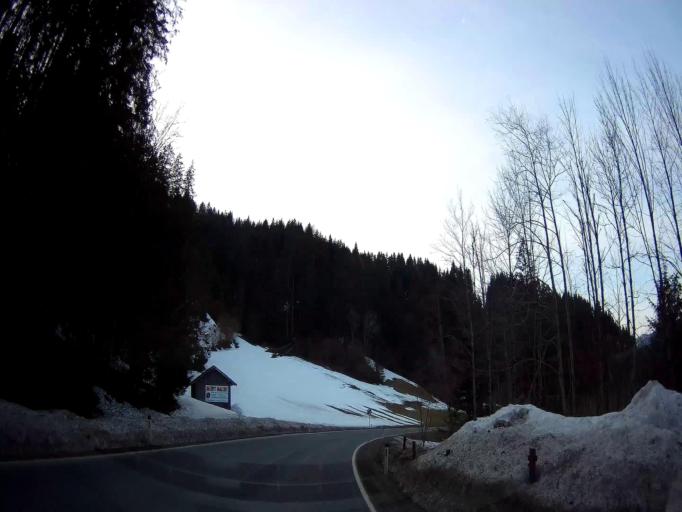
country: AT
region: Salzburg
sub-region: Politischer Bezirk Hallein
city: Abtenau
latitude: 47.5461
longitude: 13.4132
